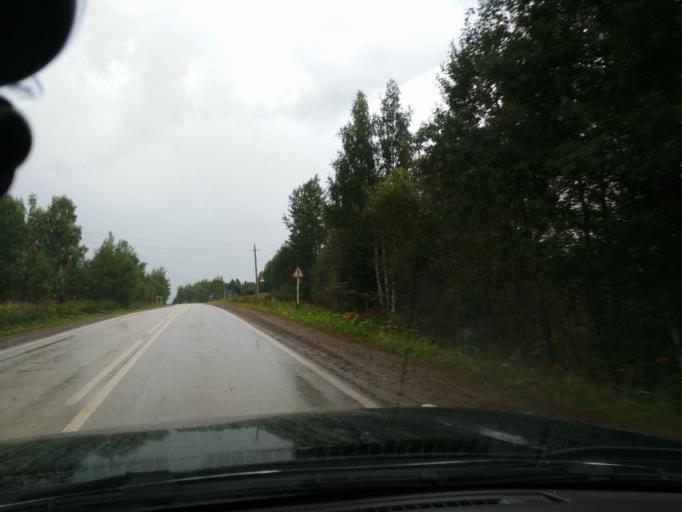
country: RU
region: Perm
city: Barda
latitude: 56.8846
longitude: 55.8335
